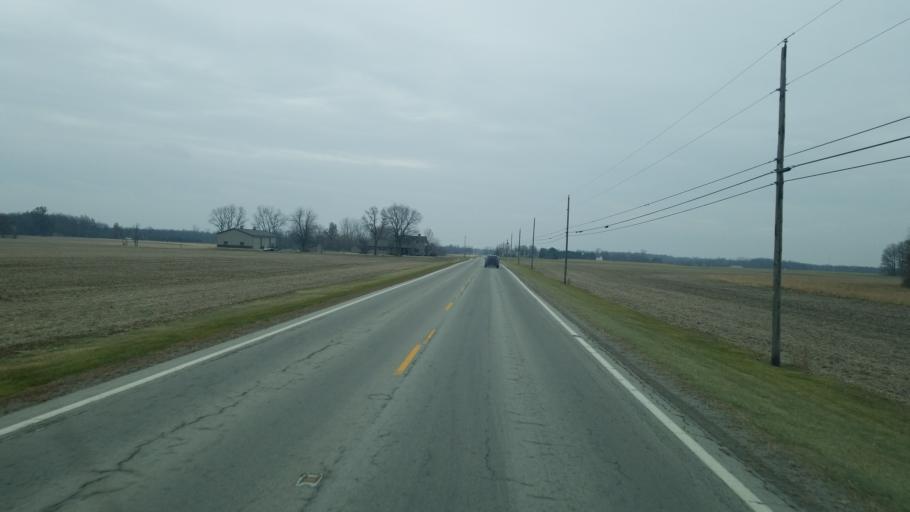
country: US
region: Ohio
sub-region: Hardin County
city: Forest
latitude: 40.7034
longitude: -83.4552
